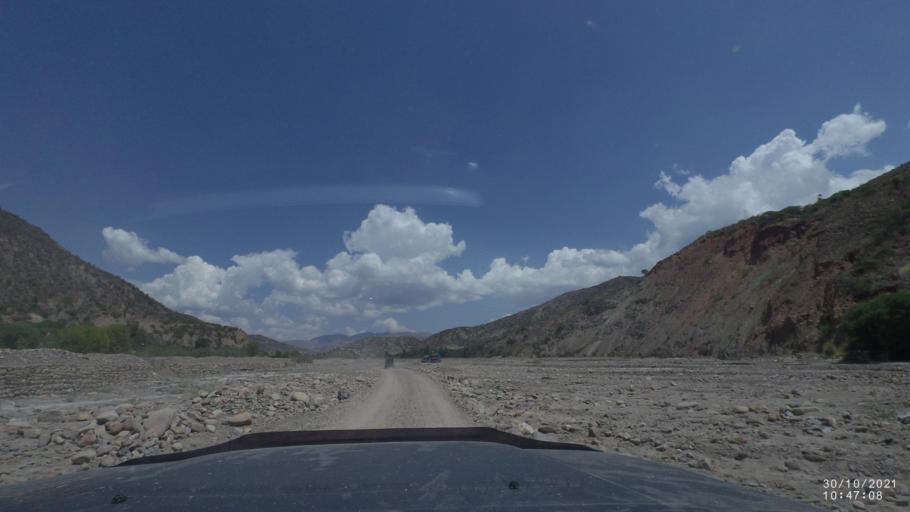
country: BO
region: Cochabamba
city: Sipe Sipe
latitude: -17.5606
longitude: -66.4600
